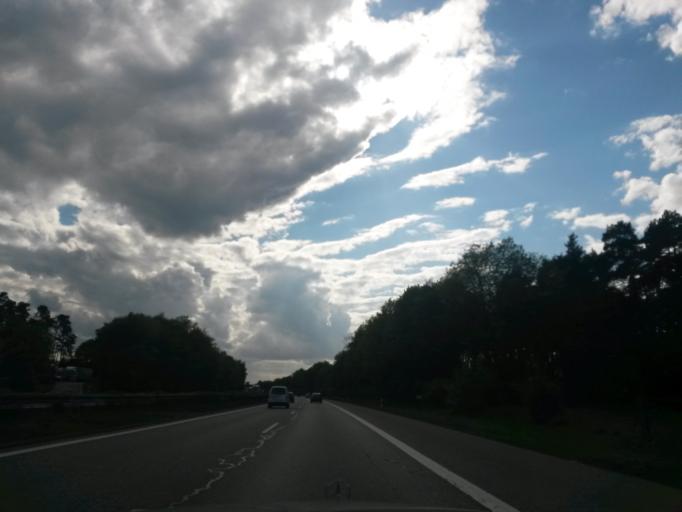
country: DE
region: Bavaria
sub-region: Regierungsbezirk Mittelfranken
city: Petersaurach
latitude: 49.3053
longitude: 10.7675
